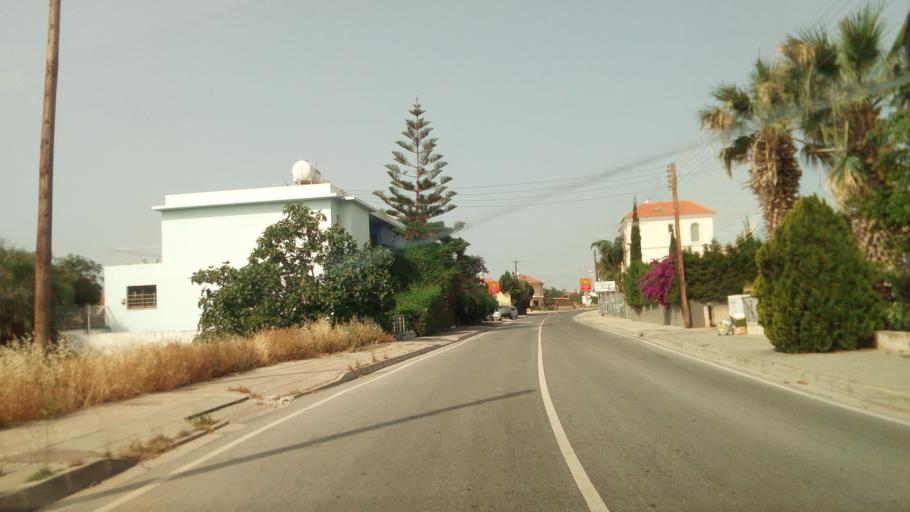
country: CY
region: Limassol
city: Ypsonas
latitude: 34.6879
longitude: 32.9794
